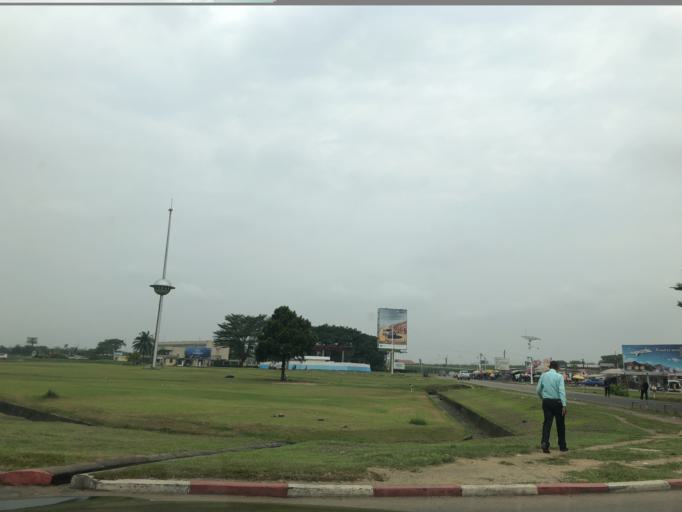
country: CM
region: Littoral
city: Douala
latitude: 4.0140
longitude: 9.7184
